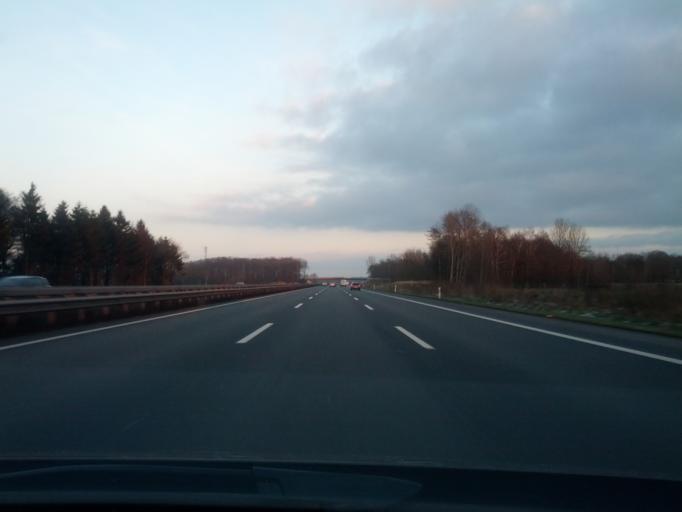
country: DE
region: Lower Saxony
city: Halvesbostel
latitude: 53.3229
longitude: 9.5875
